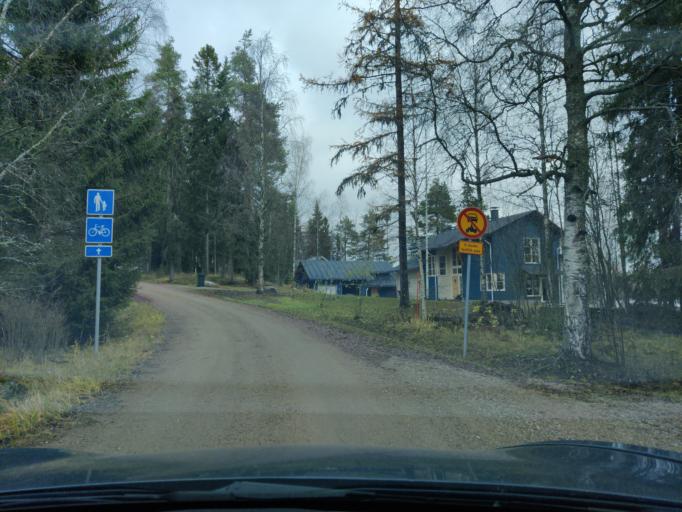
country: FI
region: Northern Savo
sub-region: Ylae-Savo
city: Kiuruvesi
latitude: 63.6438
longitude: 26.6442
